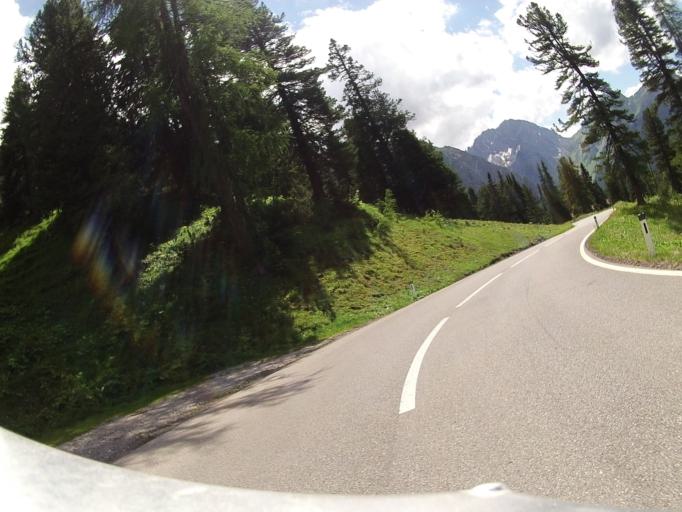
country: AT
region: Tyrol
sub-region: Politischer Bezirk Reutte
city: Namlos
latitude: 47.2857
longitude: 10.6409
